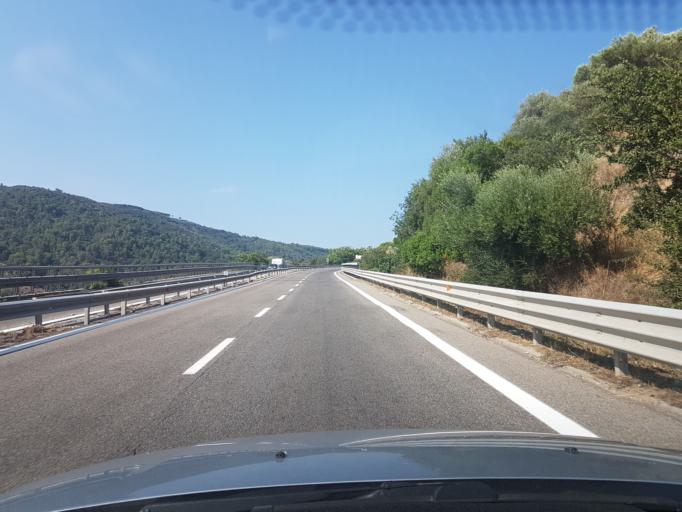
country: IT
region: Sardinia
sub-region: Provincia di Nuoro
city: Nuoro
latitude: 40.3412
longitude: 9.3111
